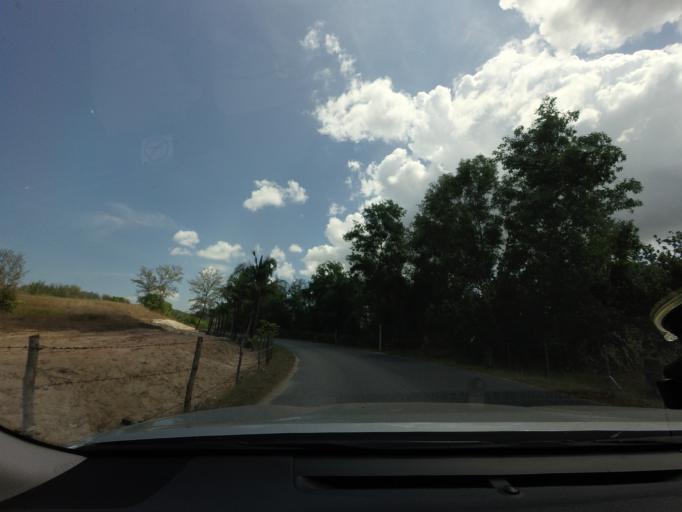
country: TH
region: Phuket
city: Thalang
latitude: 8.0334
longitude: 98.2878
